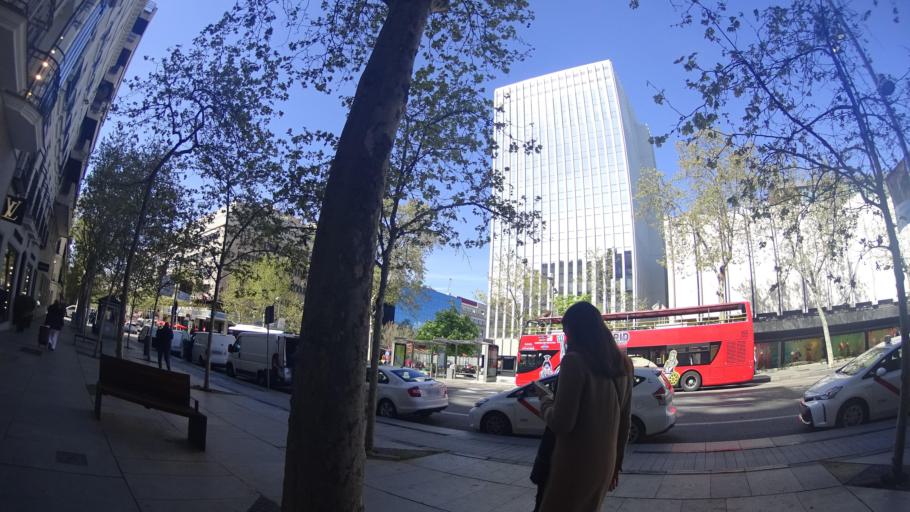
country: ES
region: Madrid
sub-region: Provincia de Madrid
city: Salamanca
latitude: 40.4298
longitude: -3.6869
